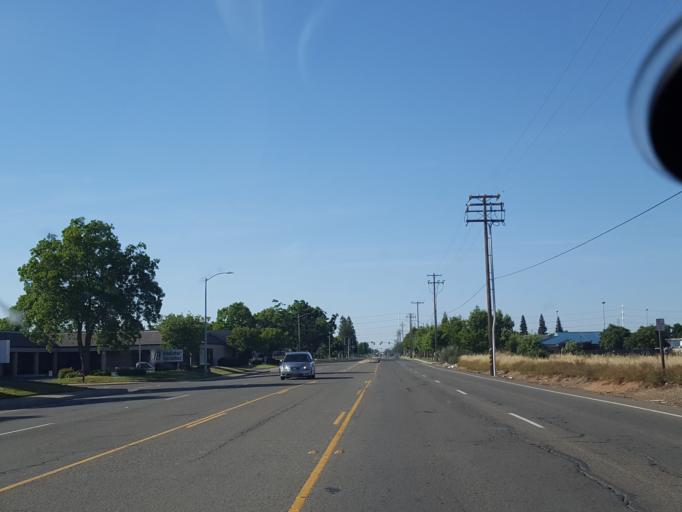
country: US
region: California
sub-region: Sacramento County
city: Florin
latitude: 38.5021
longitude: -121.3906
